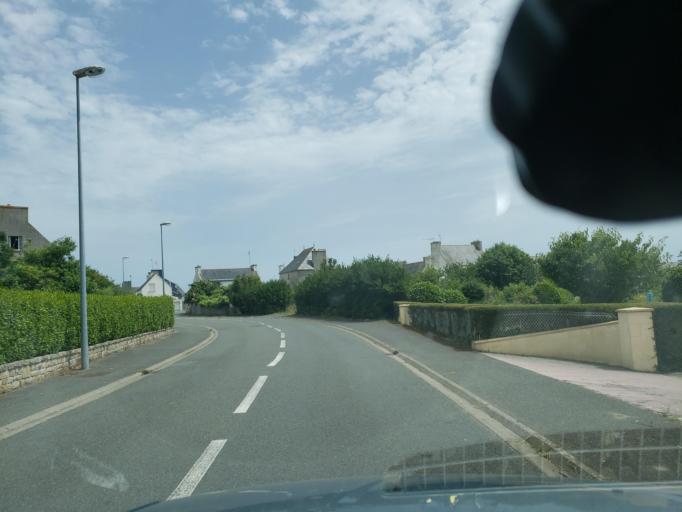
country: FR
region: Brittany
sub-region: Departement du Finistere
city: Guilvinec
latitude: 47.8011
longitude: -4.2661
